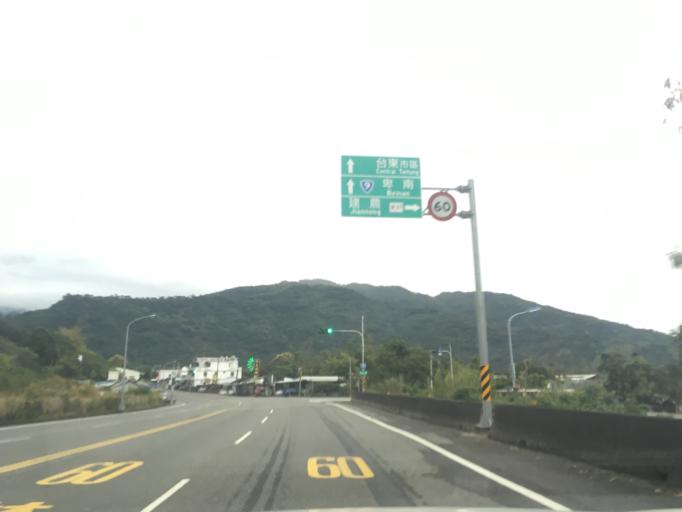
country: TW
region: Taiwan
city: Taitung City
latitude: 22.7558
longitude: 121.0530
